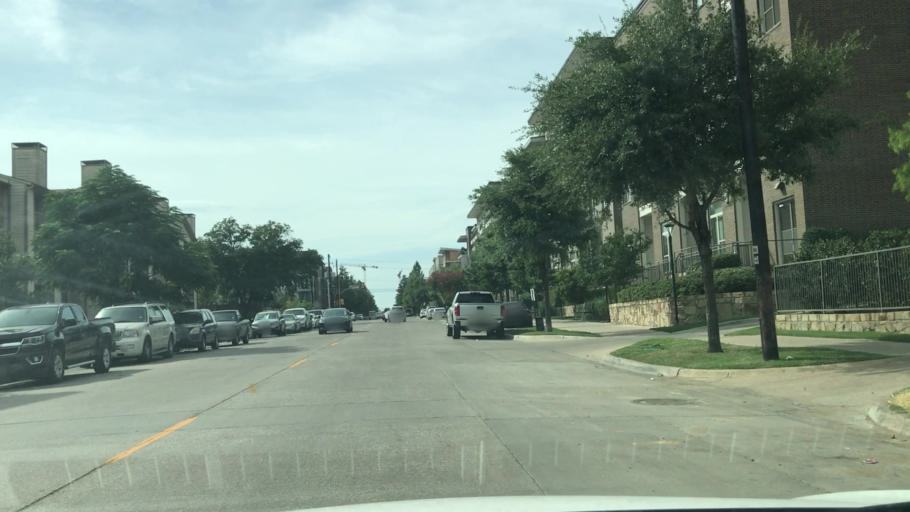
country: US
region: Texas
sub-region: Dallas County
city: Highland Park
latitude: 32.8110
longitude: -96.7798
